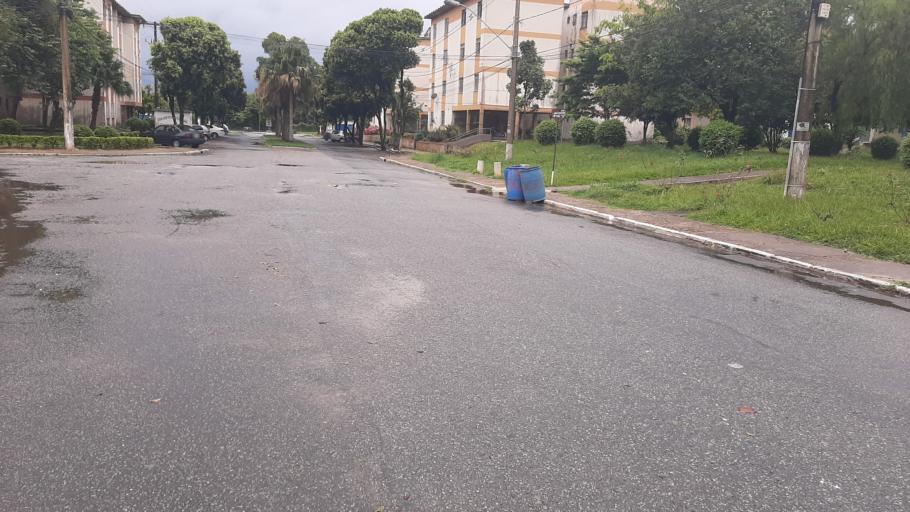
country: BR
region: Minas Gerais
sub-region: Sao Joao Del Rei
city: Sao Joao del Rei
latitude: -21.1263
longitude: -44.2357
